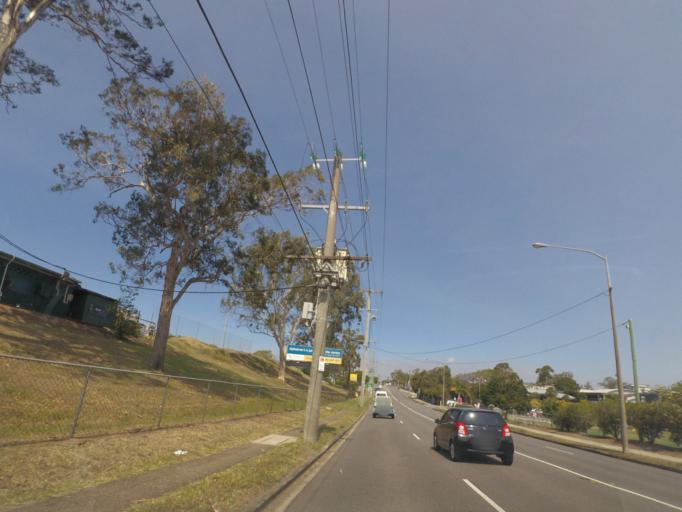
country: AU
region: Queensland
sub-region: Brisbane
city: Upper Mount Gravatt
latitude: -27.5524
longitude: 153.0762
